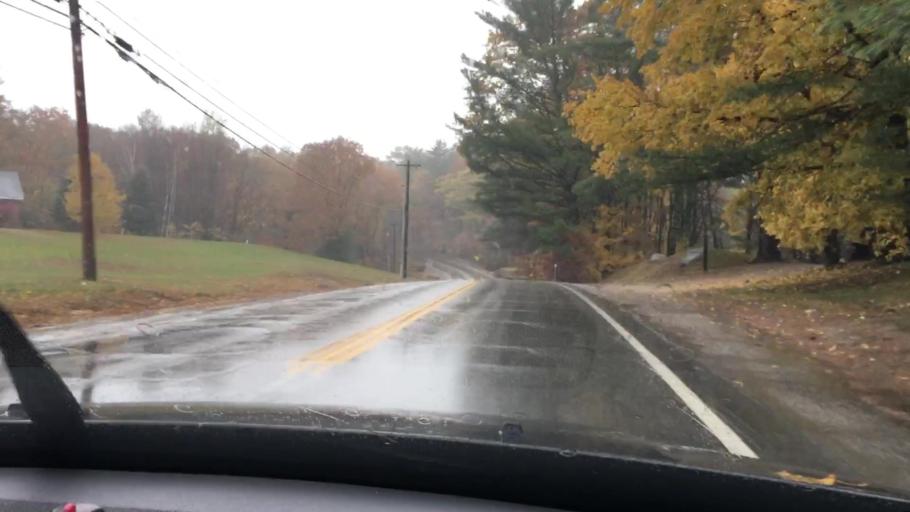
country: US
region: New Hampshire
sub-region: Belknap County
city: Meredith
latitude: 43.7117
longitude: -71.5257
